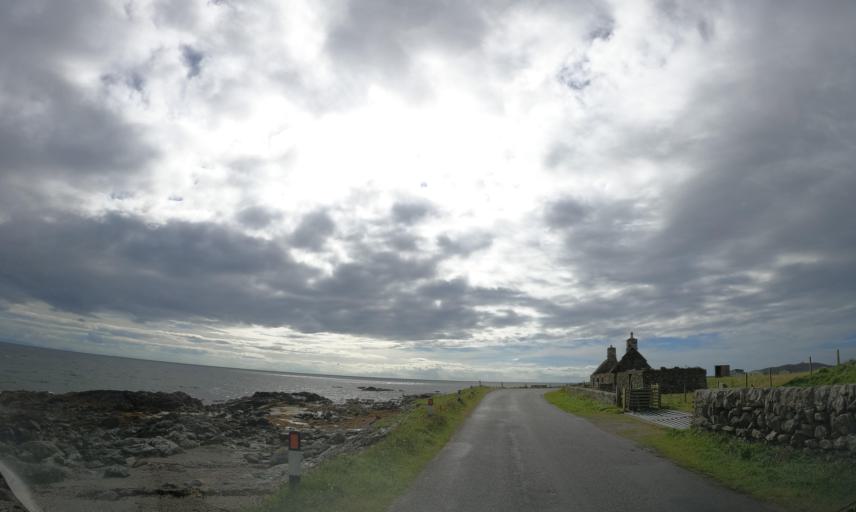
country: GB
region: Scotland
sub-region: Eilean Siar
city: Barra
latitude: 56.4863
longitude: -6.8789
